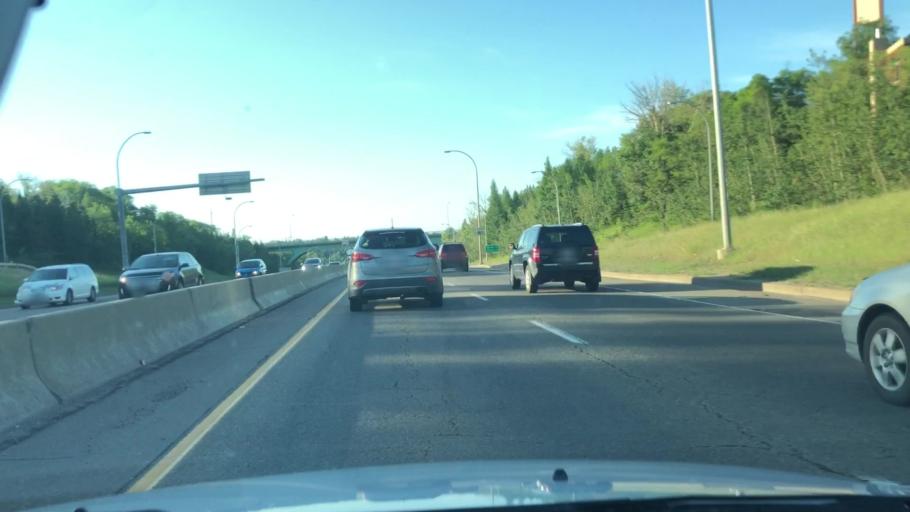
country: CA
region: Alberta
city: Edmonton
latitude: 53.5620
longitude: -113.4453
